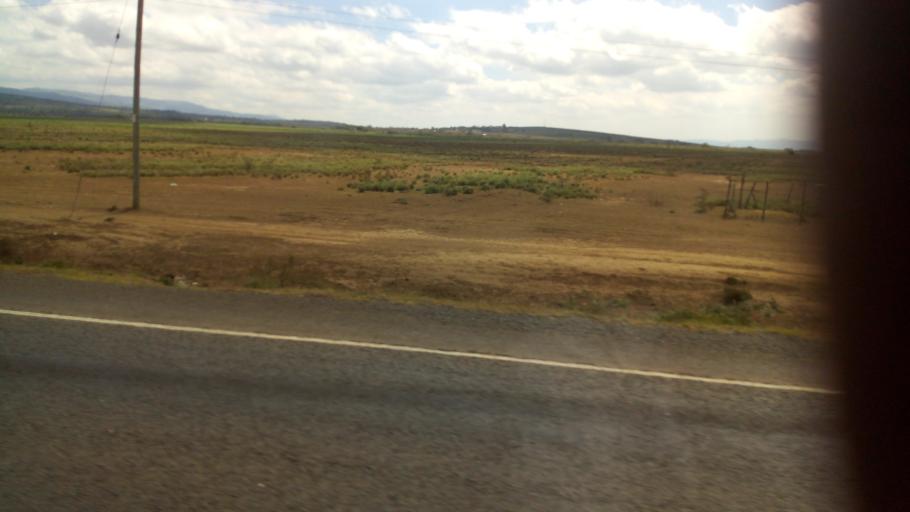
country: KE
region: Narok
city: Narok
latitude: -1.1066
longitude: 36.2329
